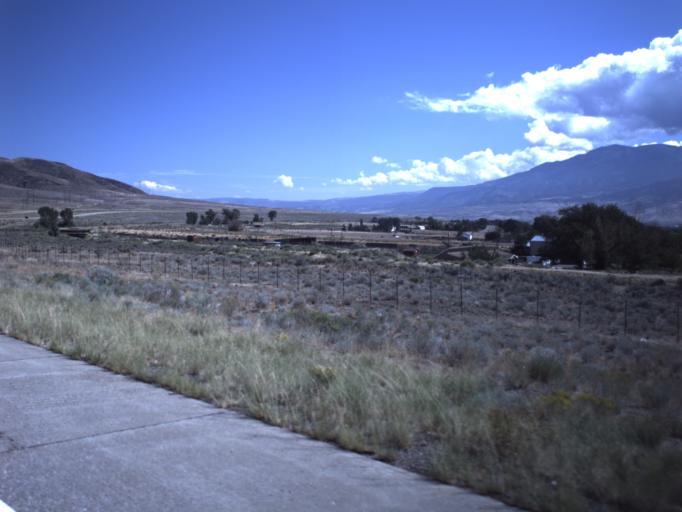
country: US
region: Utah
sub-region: Sevier County
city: Monroe
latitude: 38.6514
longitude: -112.2118
